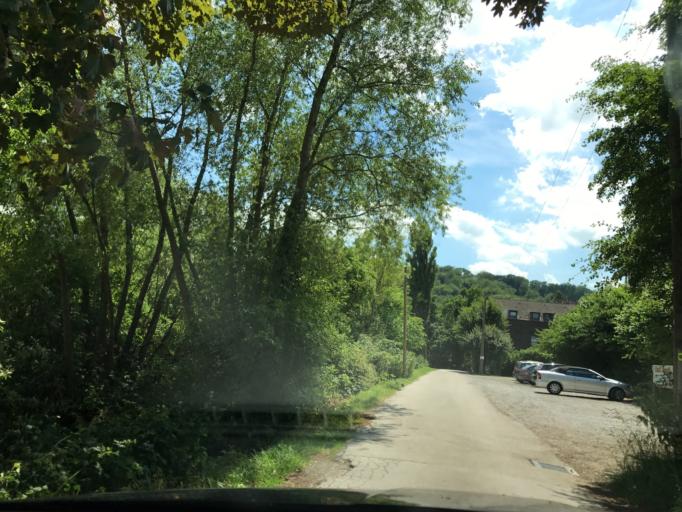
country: DE
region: North Rhine-Westphalia
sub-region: Regierungsbezirk Dusseldorf
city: Heiligenhaus
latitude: 51.3798
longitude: 6.9813
